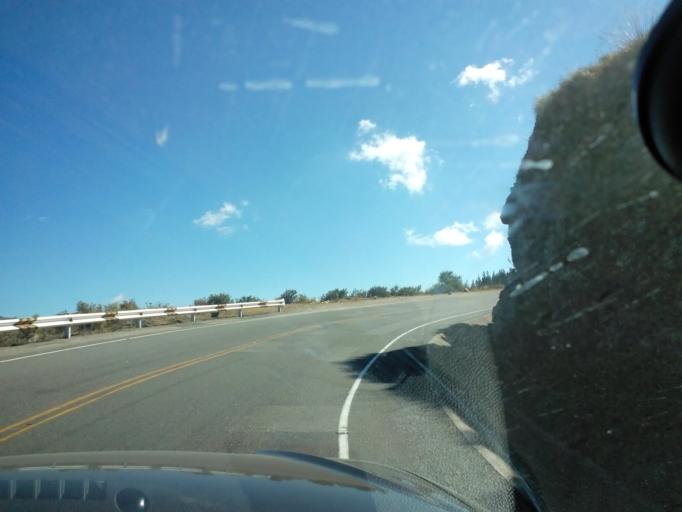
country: PE
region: Apurimac
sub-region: Provincia de Abancay
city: Tamburco
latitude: -13.5866
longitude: -72.8198
